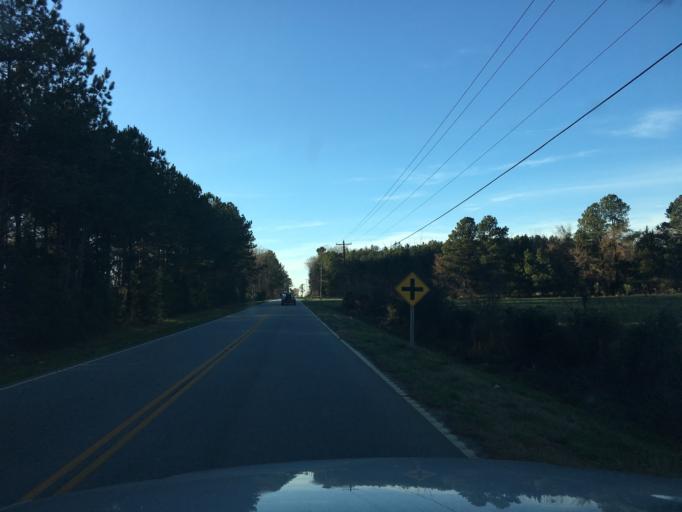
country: US
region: South Carolina
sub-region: Saluda County
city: Saluda
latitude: 34.0254
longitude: -81.7956
